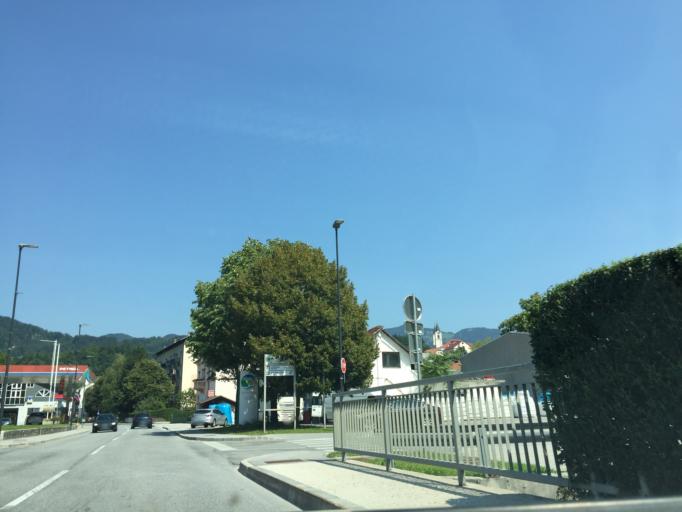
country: SI
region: Zagorje ob Savi
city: Zagorje ob Savi
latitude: 46.1286
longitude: 14.9975
